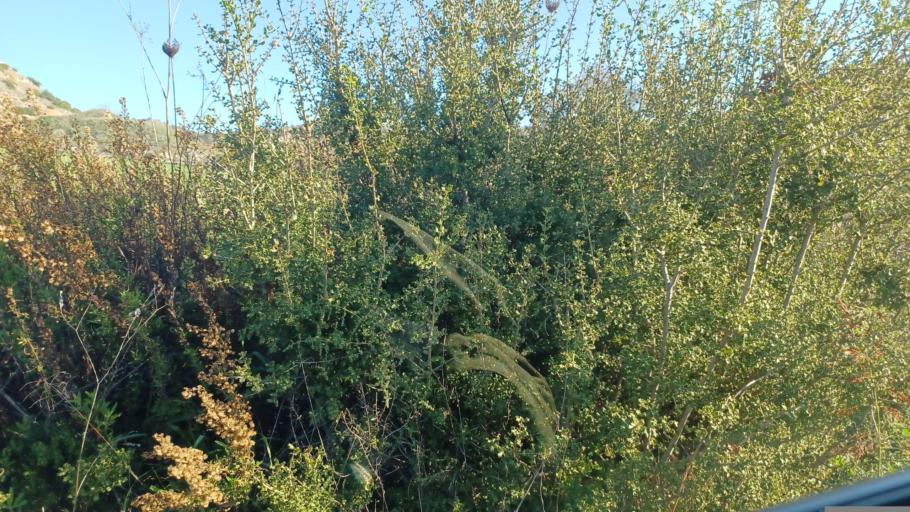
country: CY
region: Pafos
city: Mesogi
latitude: 34.8562
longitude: 32.5519
